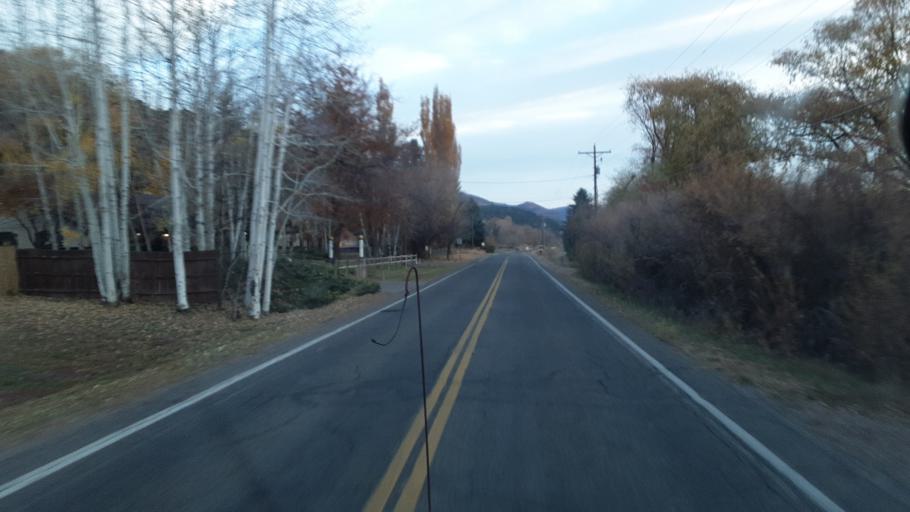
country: US
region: Colorado
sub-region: La Plata County
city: Durango
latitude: 37.3360
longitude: -107.8551
